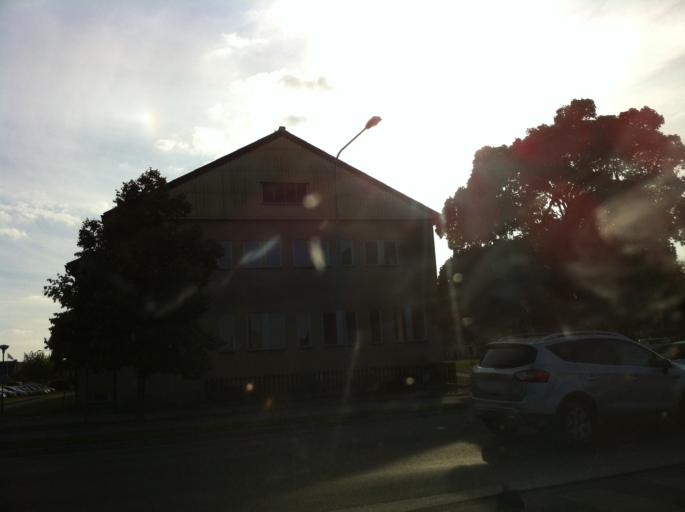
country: SE
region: Gotland
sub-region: Gotland
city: Visby
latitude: 57.6344
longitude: 18.2930
